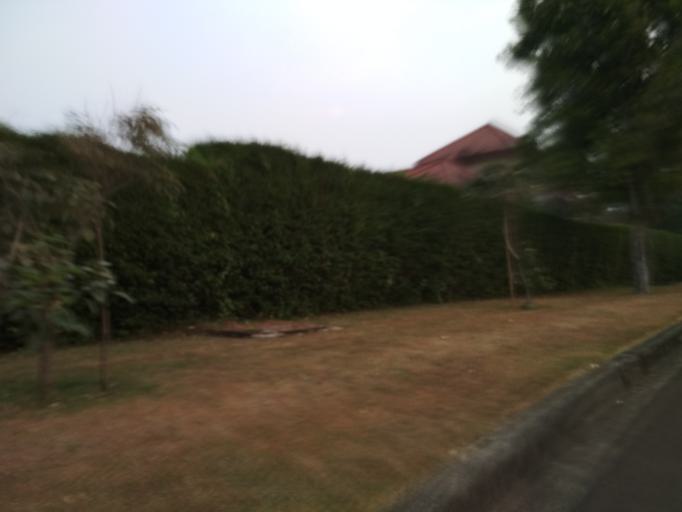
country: ID
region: West Java
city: Caringin
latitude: -6.6638
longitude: 106.8314
